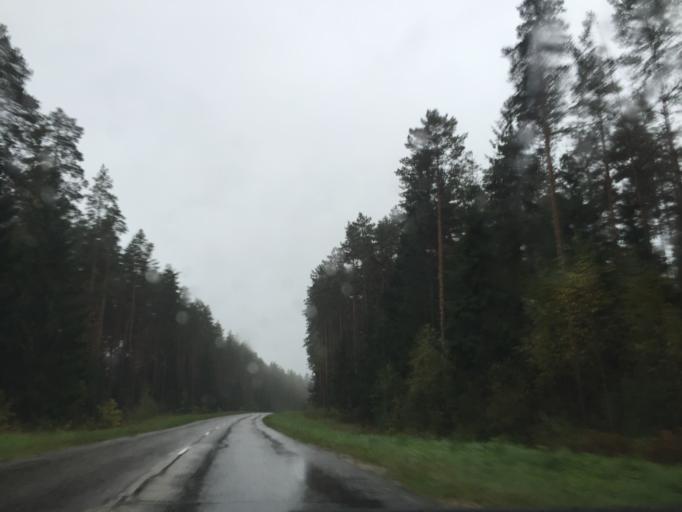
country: LV
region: Ropazu
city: Ropazi
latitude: 57.0237
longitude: 24.6828
